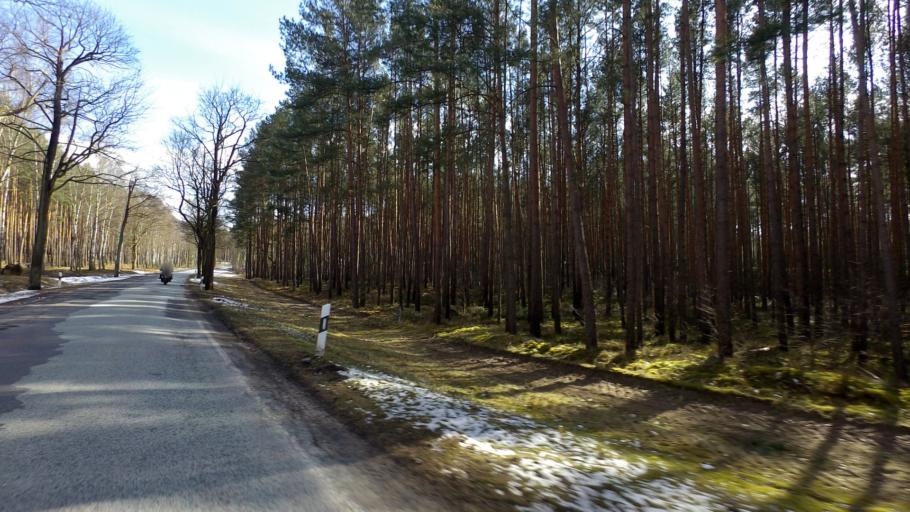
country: DE
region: Brandenburg
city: Marienwerder
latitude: 52.7930
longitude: 13.6021
